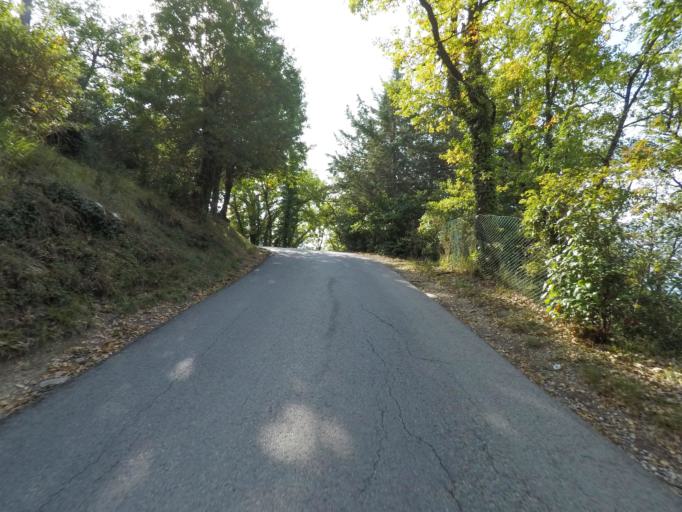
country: IT
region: Tuscany
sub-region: Provincia di Siena
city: Castellina in Chianti
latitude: 43.4249
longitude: 11.3352
